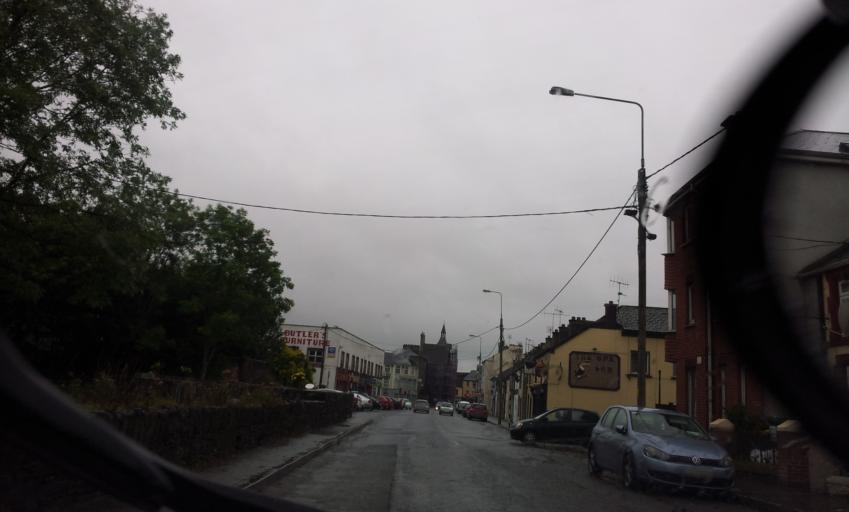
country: IE
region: Munster
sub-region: County Cork
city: Mallow
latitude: 52.1368
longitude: -8.6396
